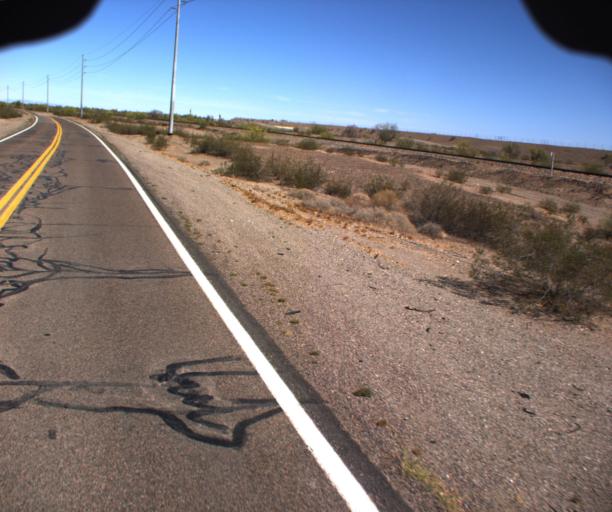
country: US
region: Arizona
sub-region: La Paz County
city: Salome
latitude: 33.7699
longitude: -113.7924
